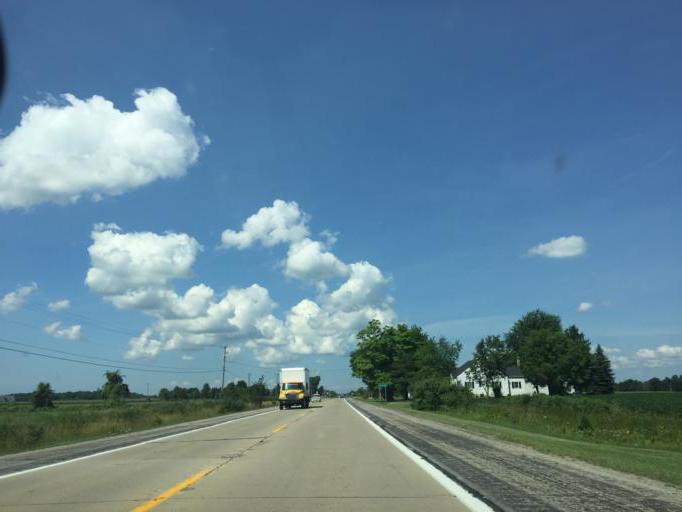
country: US
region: Ohio
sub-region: Lucas County
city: Sylvania
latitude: 41.7967
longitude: -83.7219
